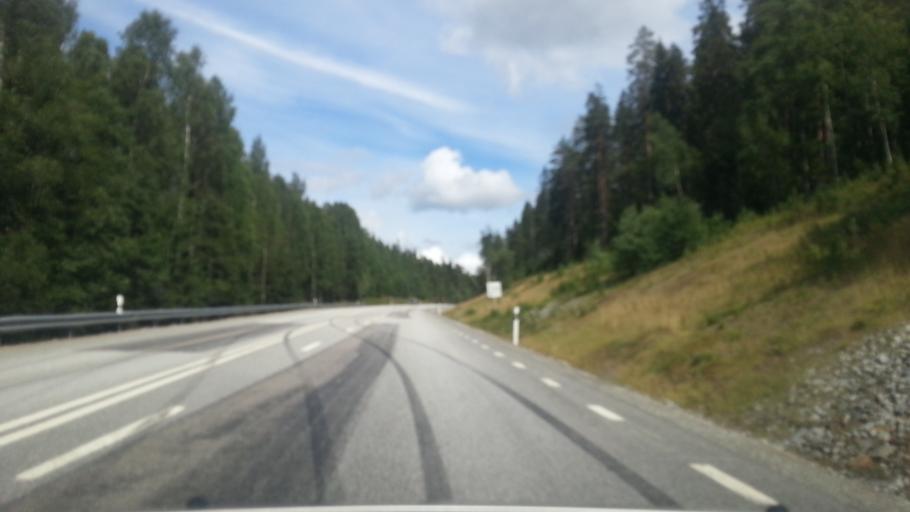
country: SE
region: Vaestmanland
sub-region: Skinnskattebergs Kommun
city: Skinnskatteberg
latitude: 59.8266
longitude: 15.5339
